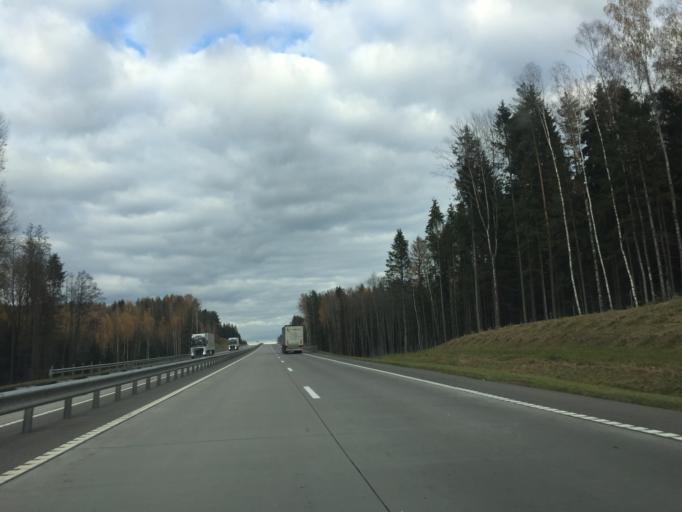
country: BY
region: Minsk
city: Rakaw
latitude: 53.9912
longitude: 27.1114
